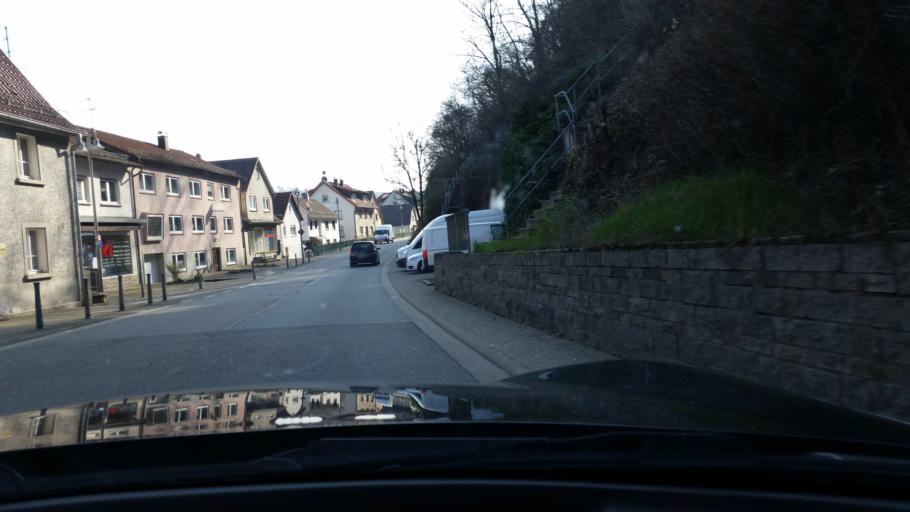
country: DE
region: Baden-Wuerttemberg
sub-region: Karlsruhe Region
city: Billigheim
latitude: 49.3503
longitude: 9.2559
